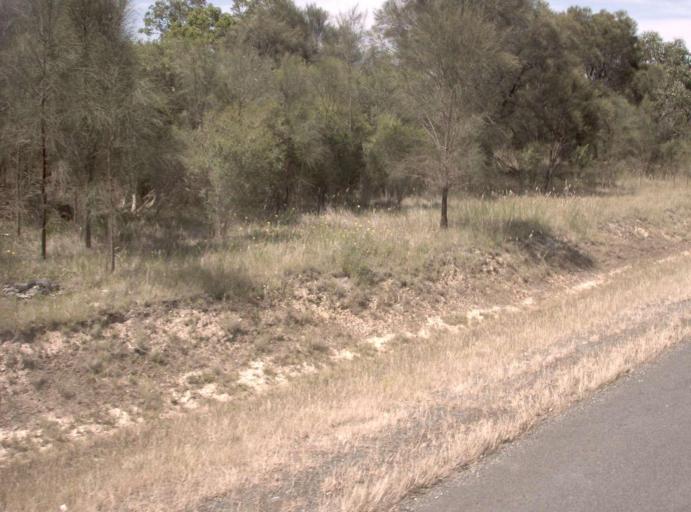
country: AU
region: Victoria
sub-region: Wellington
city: Sale
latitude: -38.1025
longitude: 146.9400
